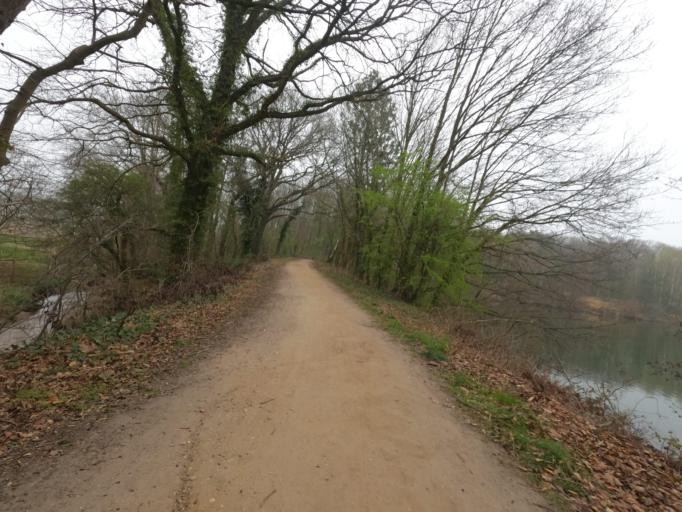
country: NL
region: Limburg
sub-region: Gemeente Roerdalen
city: Vlodrop
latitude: 51.1353
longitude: 6.0990
